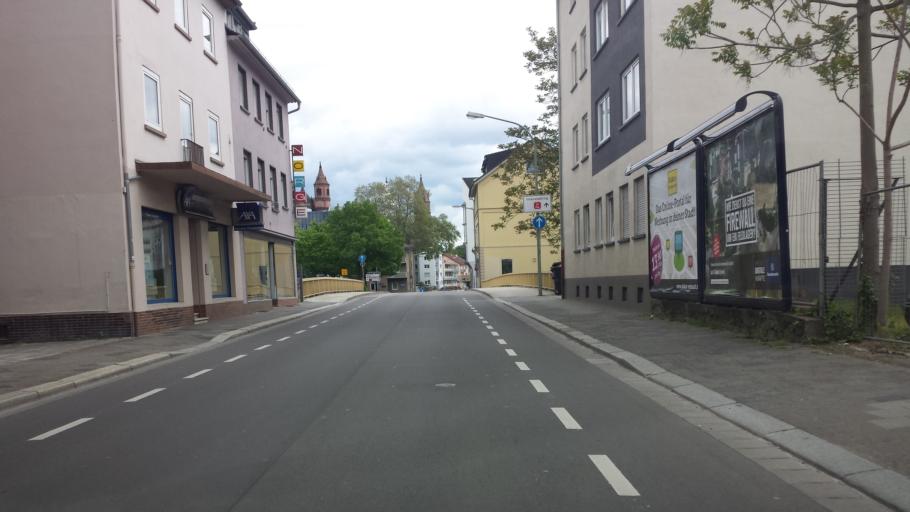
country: DE
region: Rheinland-Pfalz
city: Worms
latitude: 49.6307
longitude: 8.3539
